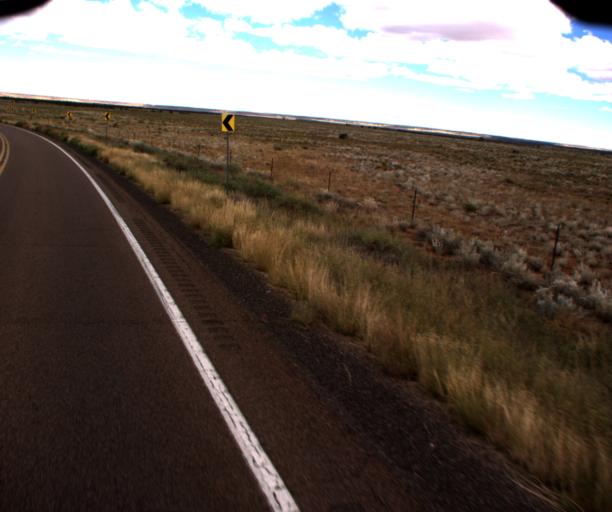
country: US
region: Arizona
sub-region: Navajo County
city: Heber-Overgaard
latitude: 34.5564
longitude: -110.4133
